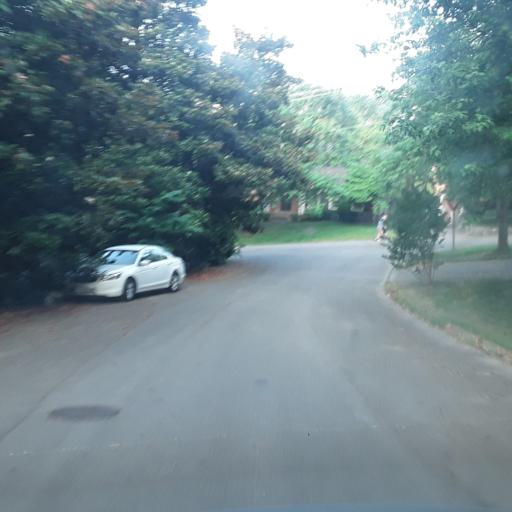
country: US
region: Tennessee
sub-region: Williamson County
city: Brentwood Estates
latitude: 36.0503
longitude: -86.7307
